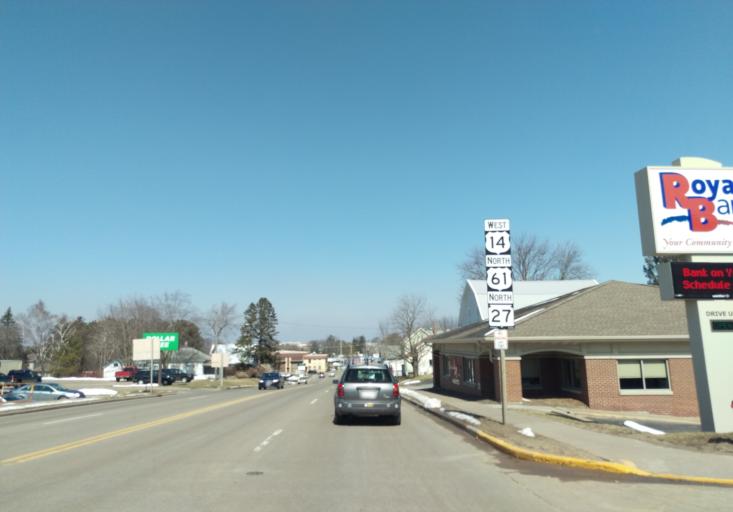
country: US
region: Wisconsin
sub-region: Vernon County
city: Viroqua
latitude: 43.5580
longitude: -90.8893
